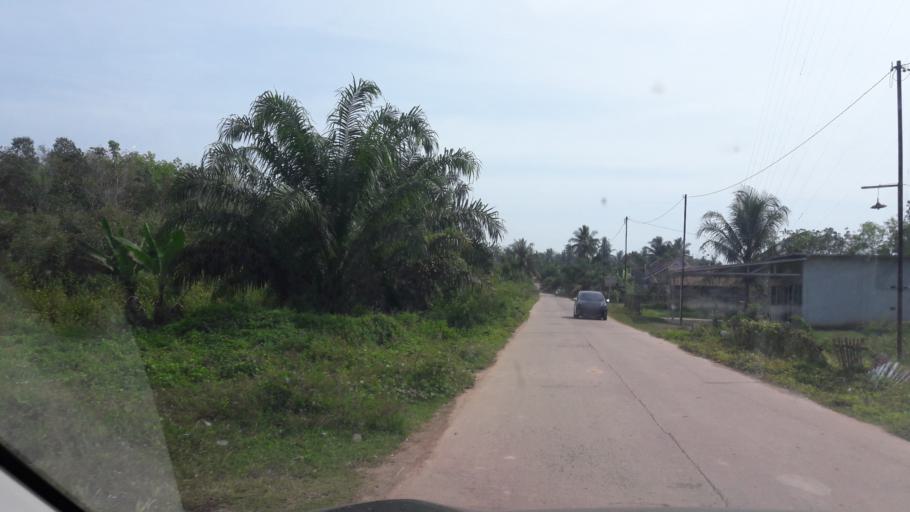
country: ID
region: South Sumatra
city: Gunungmenang
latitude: -3.3149
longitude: 104.1137
